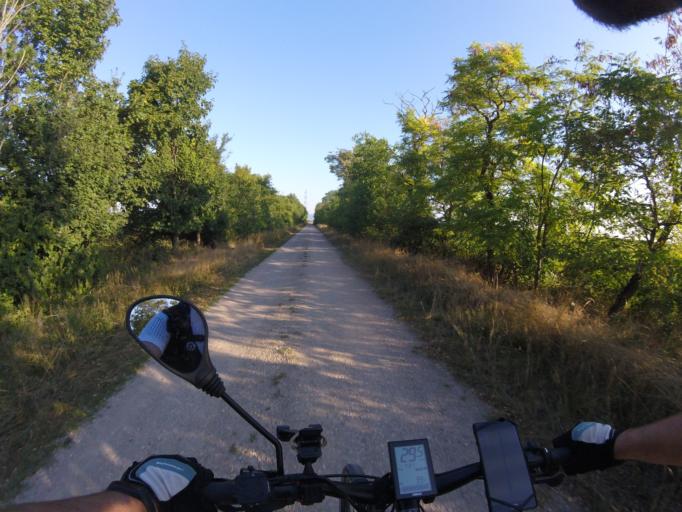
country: AT
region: Lower Austria
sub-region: Politischer Bezirk Baden
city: Trumau
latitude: 47.9734
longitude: 16.3662
